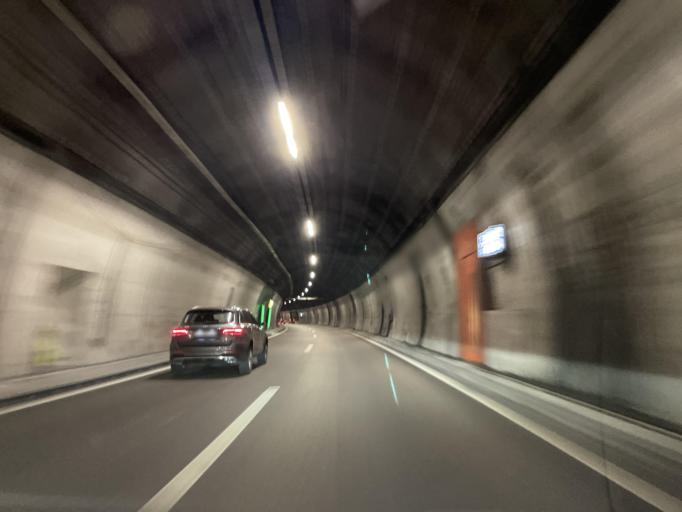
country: CH
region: Ticino
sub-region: Lugano District
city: Melide
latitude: 45.9600
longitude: 8.9441
